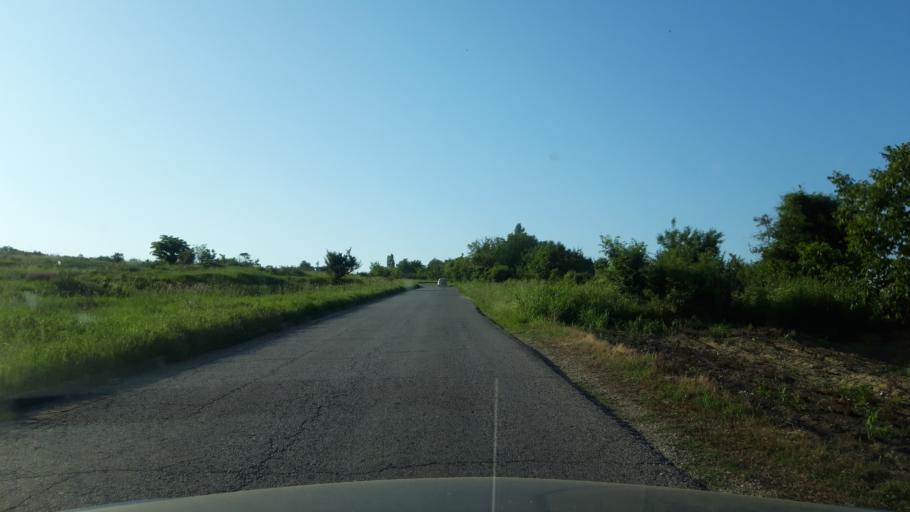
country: RS
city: Celarevo
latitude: 45.1290
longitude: 19.5073
